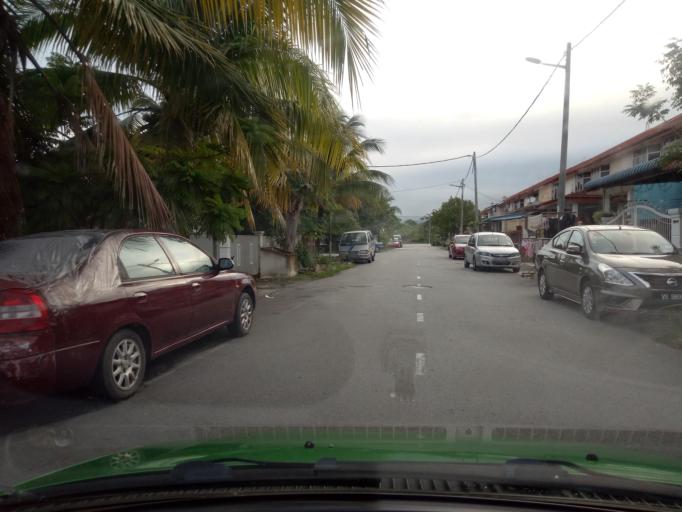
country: MY
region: Selangor
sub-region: Hulu Langat
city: Semenyih
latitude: 2.9303
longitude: 101.8629
